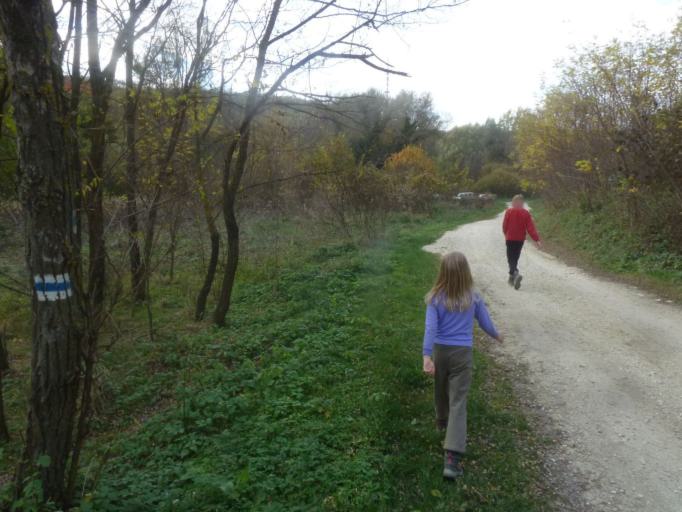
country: HU
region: Zala
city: Nagykanizsa
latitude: 46.5600
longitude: 17.0339
